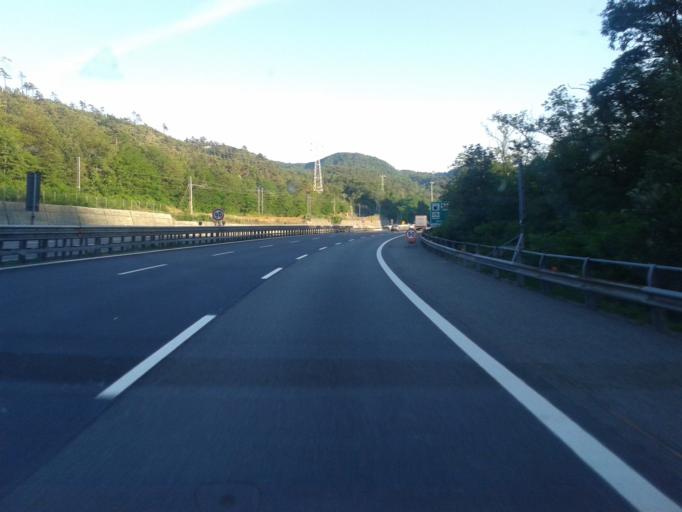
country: IT
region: Piedmont
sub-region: Provincia di Alessandria
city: Belforte Monferrato
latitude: 44.6000
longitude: 8.6668
